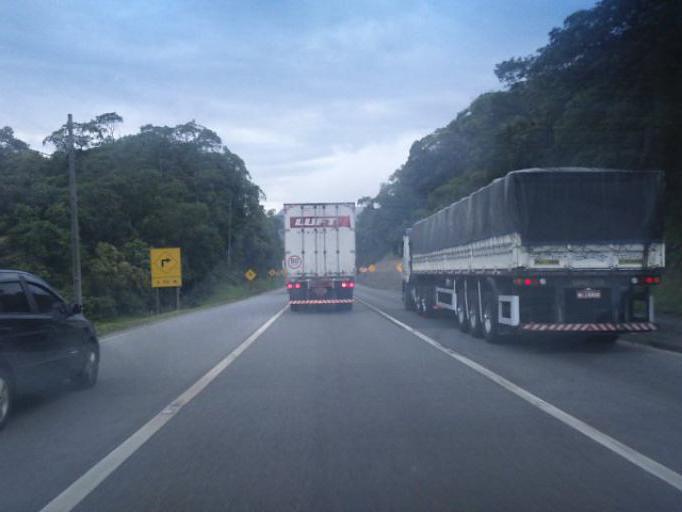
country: BR
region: Parana
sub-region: Guaratuba
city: Guaratuba
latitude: -25.8574
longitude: -48.9515
